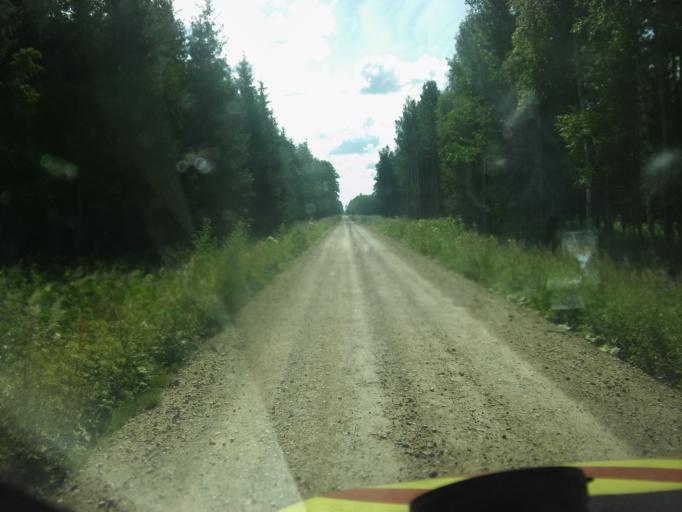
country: EE
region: Paernumaa
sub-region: Sindi linn
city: Sindi
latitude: 58.2689
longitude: 24.7331
